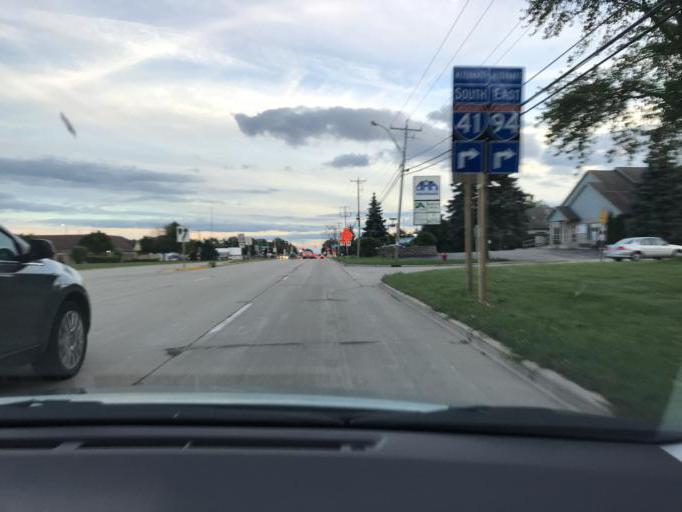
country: US
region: Wisconsin
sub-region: Kenosha County
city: Somers
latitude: 42.5918
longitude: -87.8817
